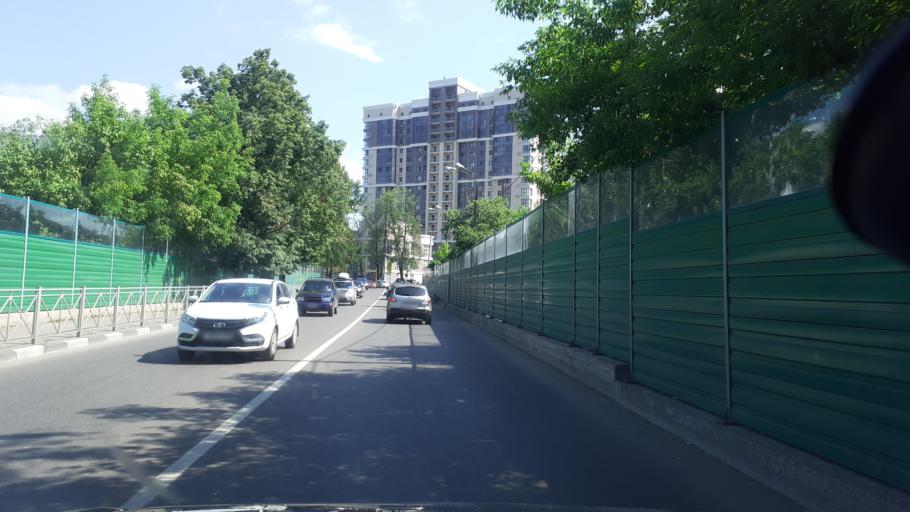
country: RU
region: Moskovskaya
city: Naro-Fominsk
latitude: 55.3856
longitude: 36.7392
